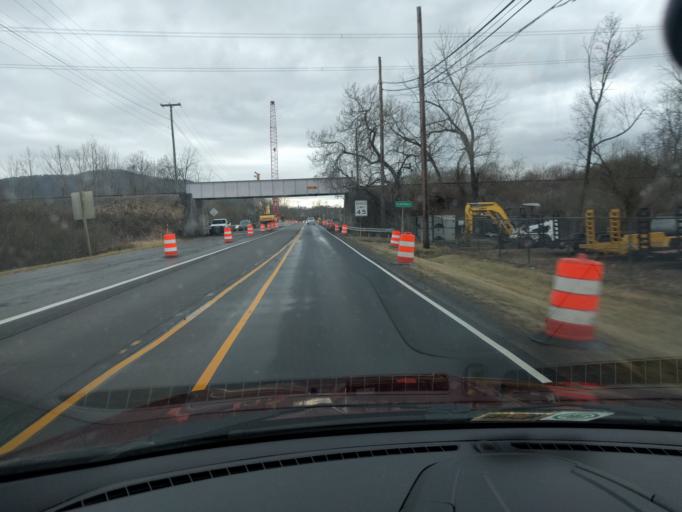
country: US
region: Virginia
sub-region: Botetourt County
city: Cloverdale
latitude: 37.3749
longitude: -79.9048
